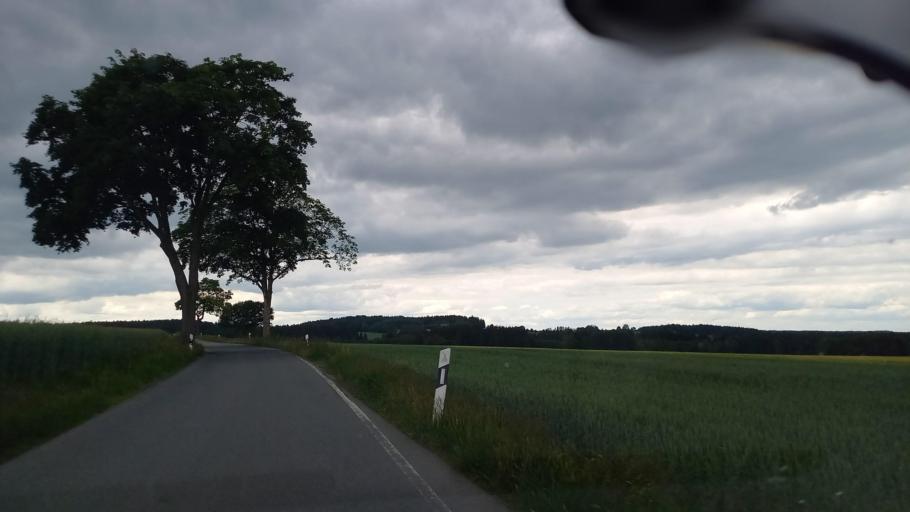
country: DE
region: Saxony
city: Hirschfeld
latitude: 50.5831
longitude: 12.4457
